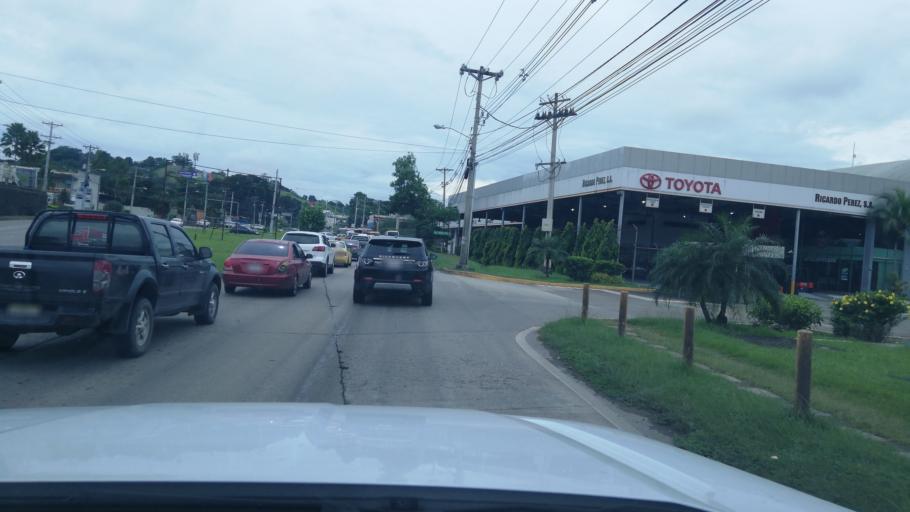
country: PA
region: Panama
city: Las Cumbres
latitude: 9.0713
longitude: -79.5222
